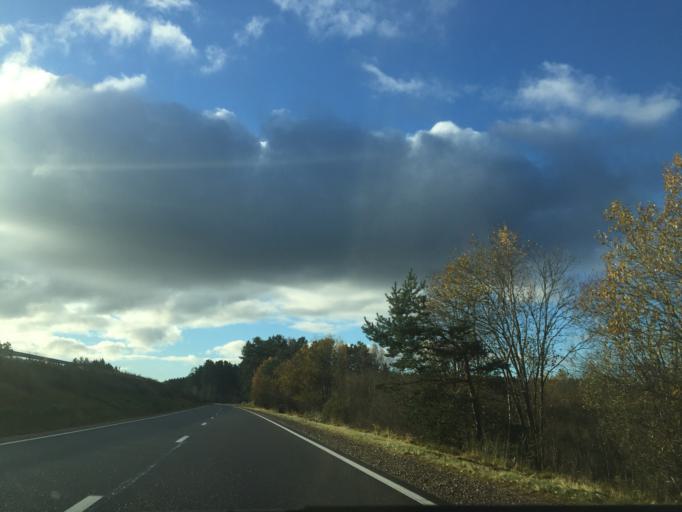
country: LV
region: Babite
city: Pinki
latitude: 56.9259
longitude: 23.9148
